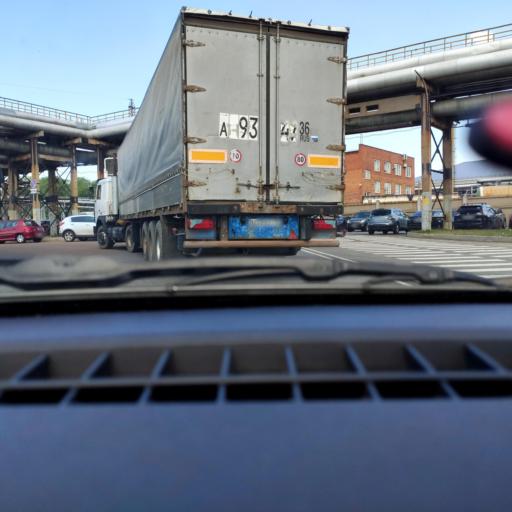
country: RU
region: Bashkortostan
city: Ufa
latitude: 54.8749
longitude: 56.1022
